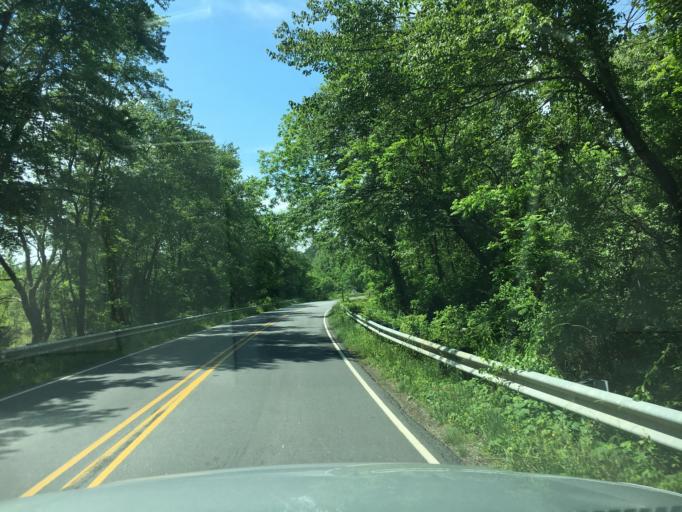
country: US
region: North Carolina
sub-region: Henderson County
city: Fletcher
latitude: 35.4000
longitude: -82.5177
